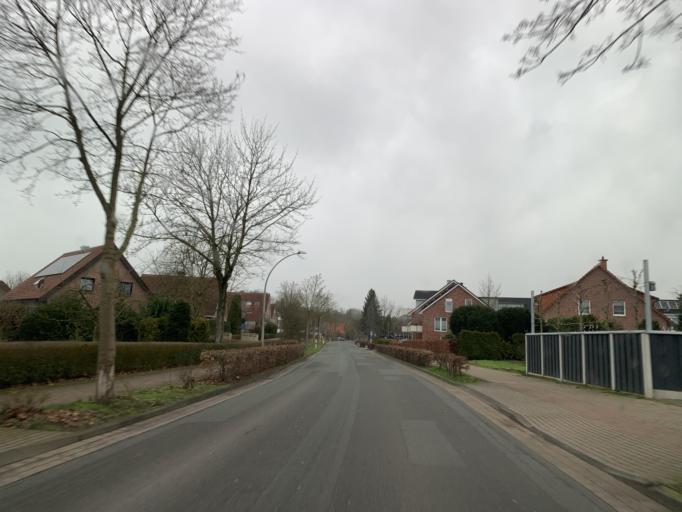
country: DE
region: North Rhine-Westphalia
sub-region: Regierungsbezirk Munster
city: Senden
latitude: 51.8546
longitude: 7.4672
